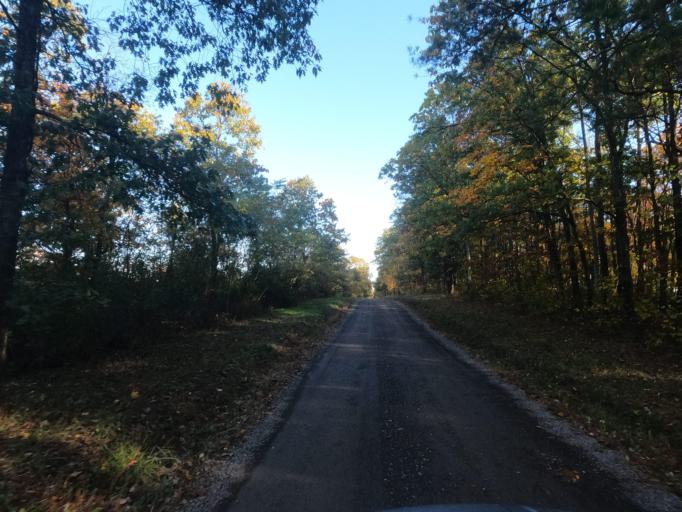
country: US
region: West Virginia
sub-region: Morgan County
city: Berkeley Springs
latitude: 39.6316
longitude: -78.4811
